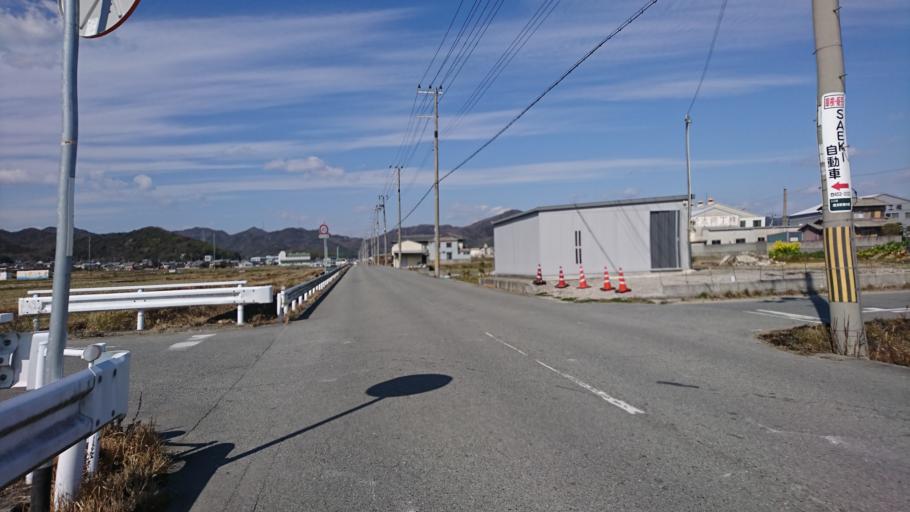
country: JP
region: Hyogo
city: Kakogawacho-honmachi
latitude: 34.8065
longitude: 134.8102
